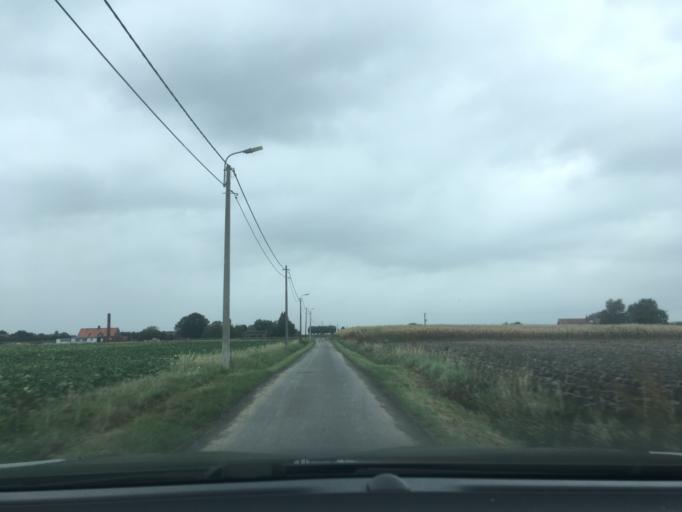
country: BE
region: Flanders
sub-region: Provincie West-Vlaanderen
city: Ledegem
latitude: 50.8839
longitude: 3.1327
